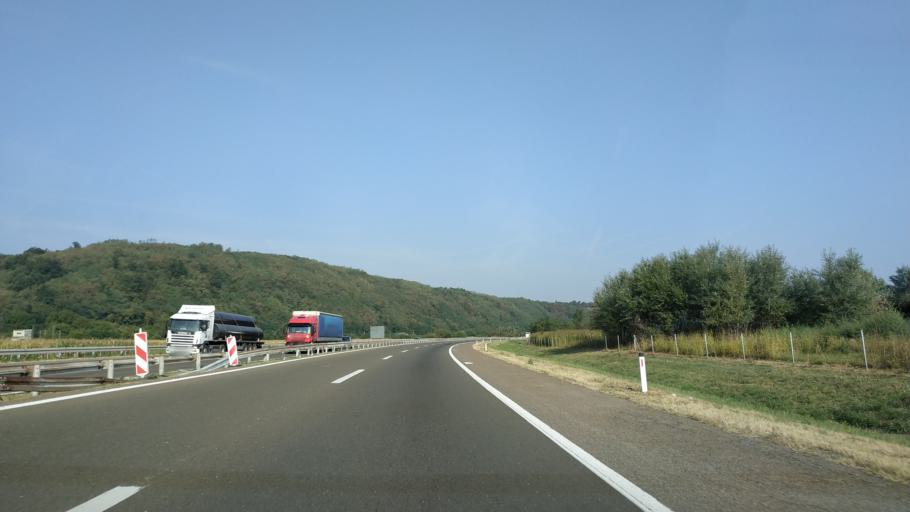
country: RS
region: Central Serbia
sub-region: Sumadijski Okrug
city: Batocina
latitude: 44.0902
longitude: 21.1729
